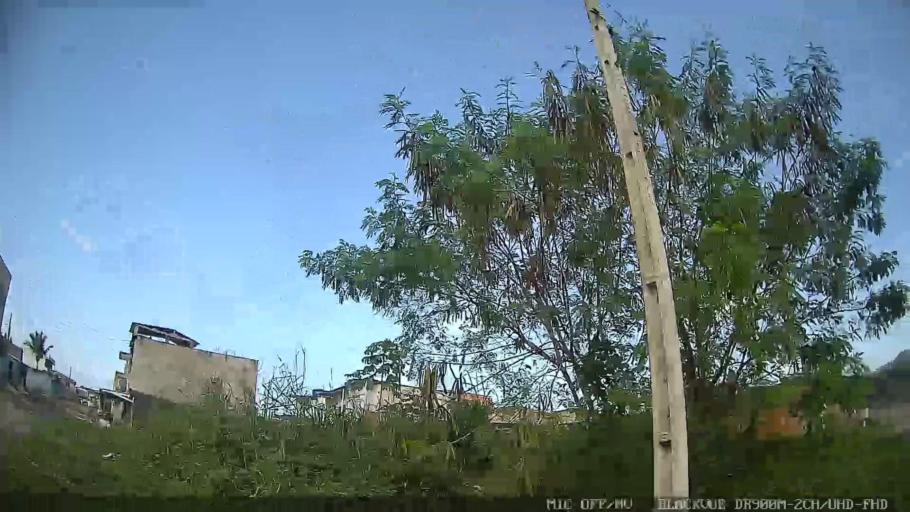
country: BR
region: Sao Paulo
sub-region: Guaruja
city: Guaruja
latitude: -23.9740
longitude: -46.2141
